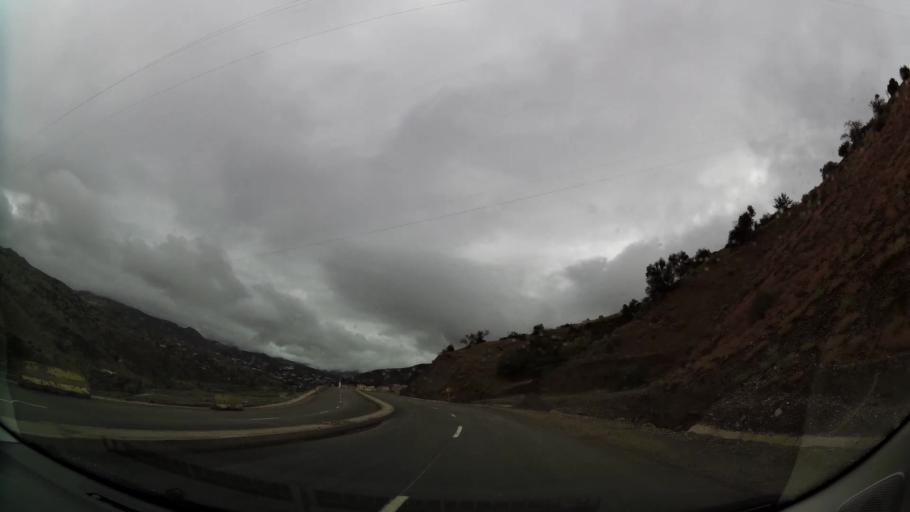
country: MA
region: Taza-Al Hoceima-Taounate
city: Imzourene
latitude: 34.9756
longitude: -3.8123
